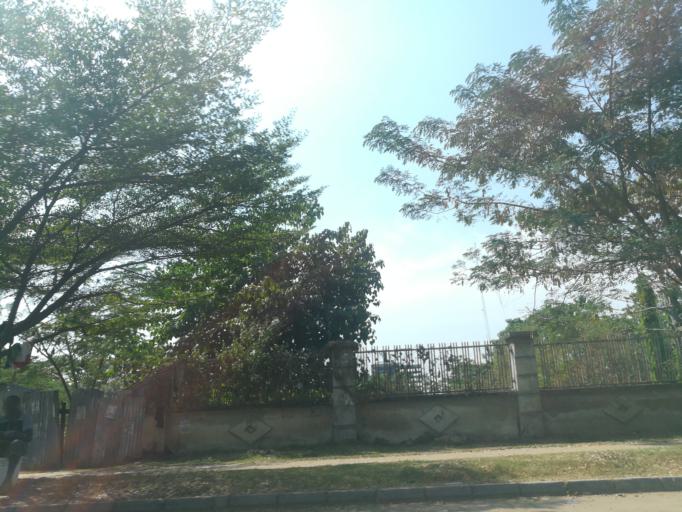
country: NG
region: Abuja Federal Capital Territory
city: Abuja
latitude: 9.0687
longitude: 7.4369
